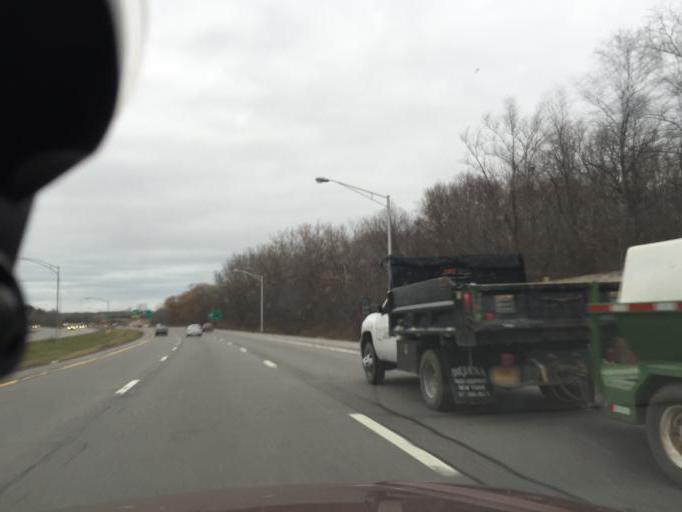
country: US
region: New York
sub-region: Monroe County
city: Greece
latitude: 43.2010
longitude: -77.6776
